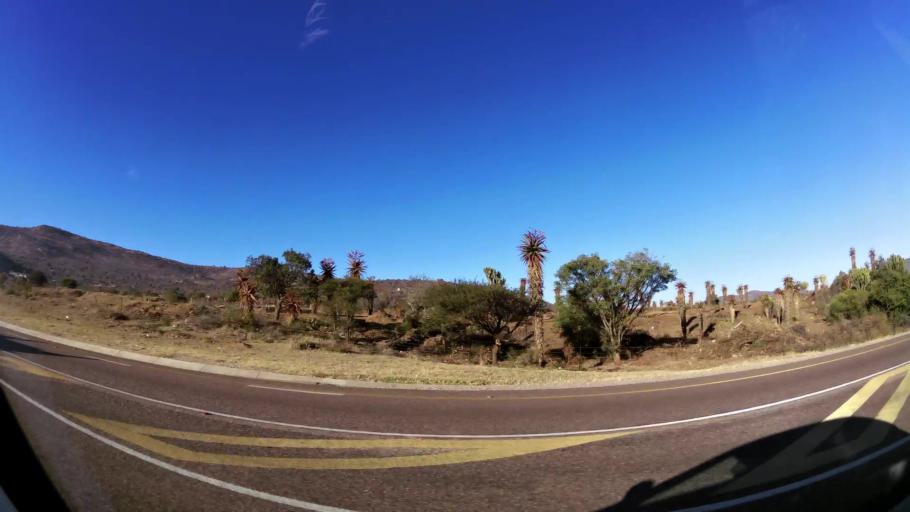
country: ZA
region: Limpopo
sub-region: Capricorn District Municipality
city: Mankoeng
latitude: -23.9427
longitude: 29.8121
